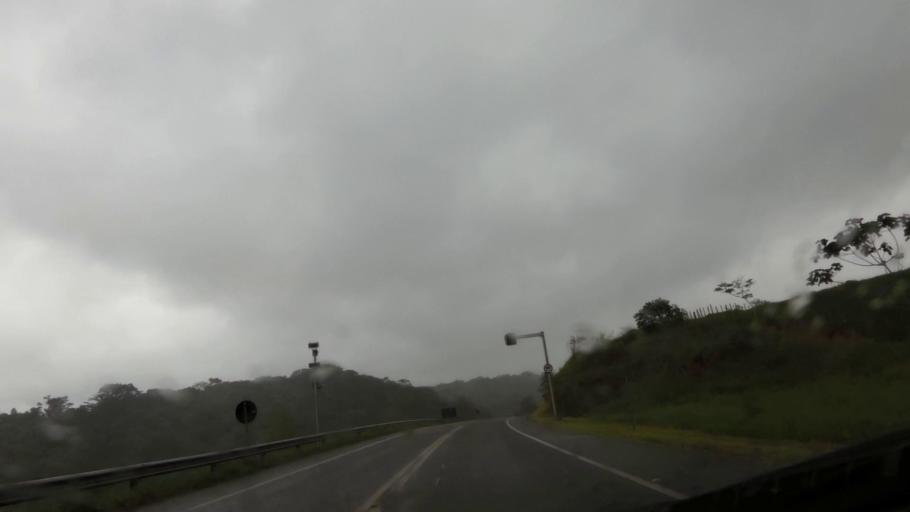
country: BR
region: Espirito Santo
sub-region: Guarapari
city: Guarapari
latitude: -20.6390
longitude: -40.5301
